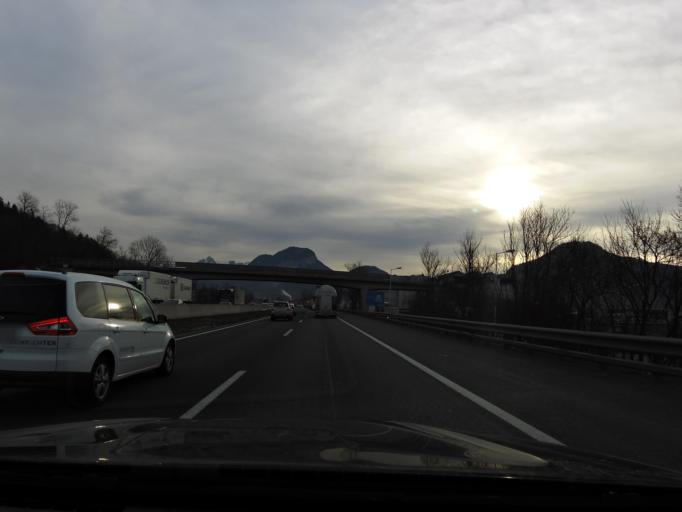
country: AT
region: Tyrol
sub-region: Politischer Bezirk Kufstein
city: Worgl
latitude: 47.4848
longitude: 12.0351
